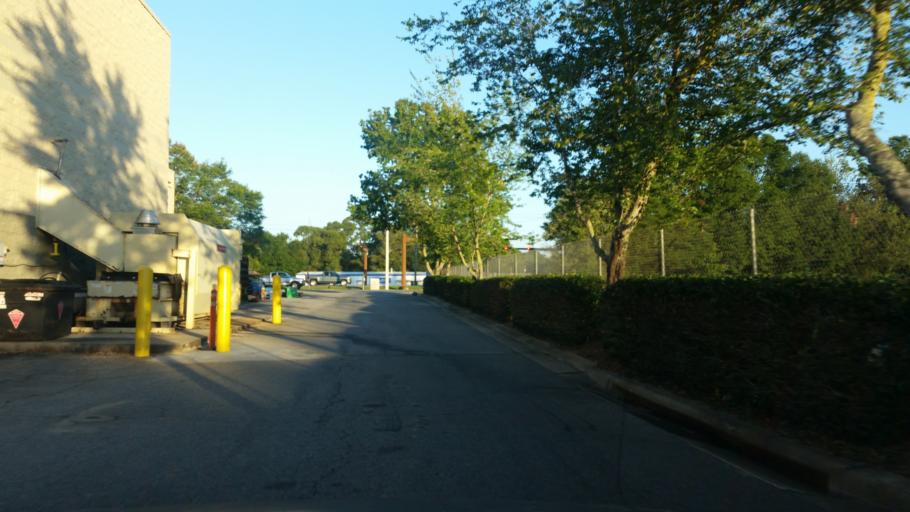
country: US
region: Florida
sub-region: Escambia County
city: Ensley
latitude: 30.5365
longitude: -87.3120
